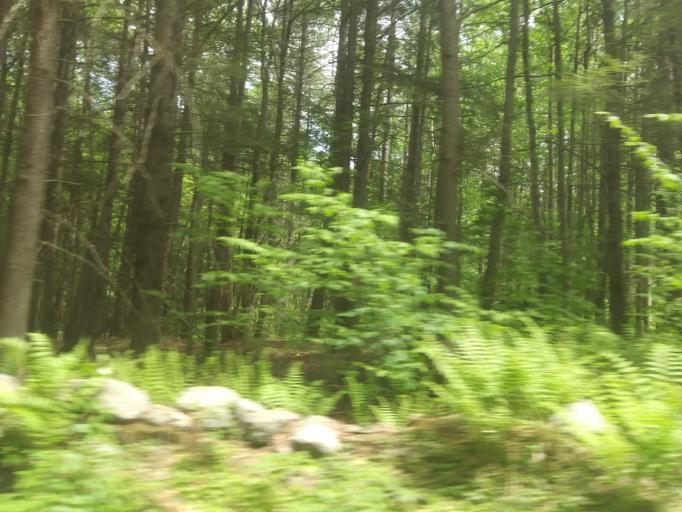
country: US
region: Massachusetts
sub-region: Franklin County
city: Shelburne Falls
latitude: 42.5945
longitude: -72.7623
